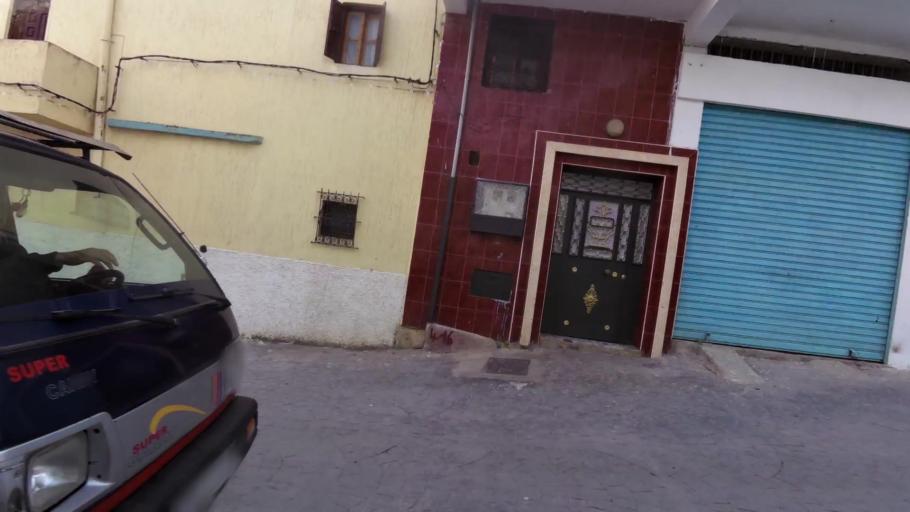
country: MA
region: Tanger-Tetouan
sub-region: Tetouan
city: Martil
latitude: 35.6839
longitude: -5.3301
